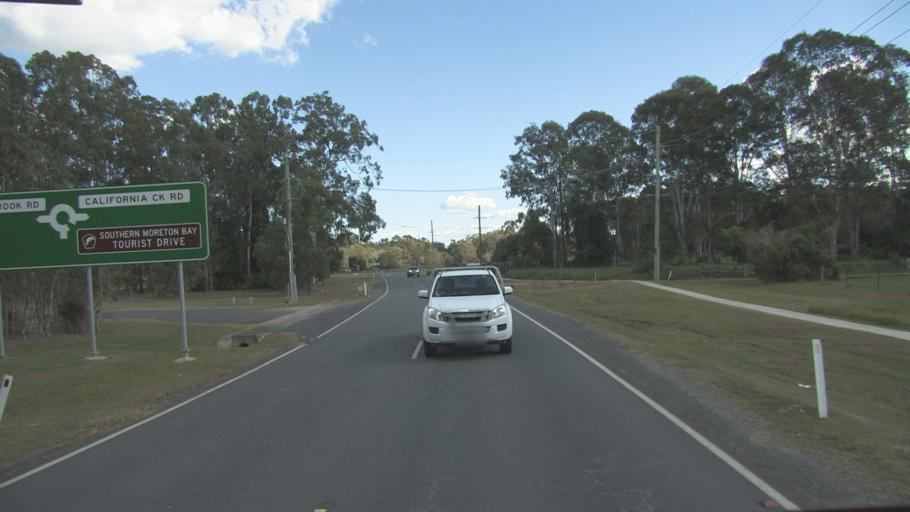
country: AU
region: Queensland
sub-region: Logan
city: Beenleigh
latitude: -27.6629
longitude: 153.2145
